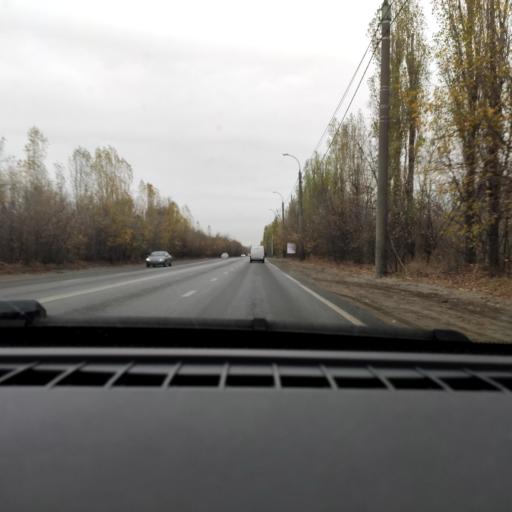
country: RU
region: Voronezj
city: Maslovka
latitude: 51.6037
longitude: 39.2542
